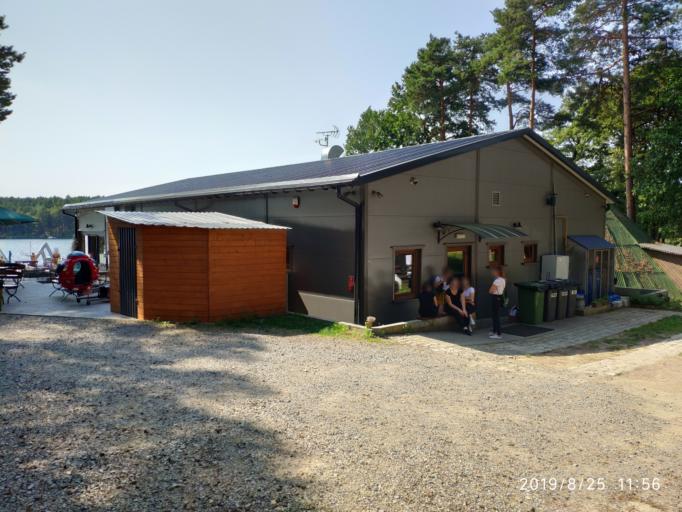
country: PL
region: Lubusz
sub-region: Powiat krosnienski
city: Dabie
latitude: 51.9988
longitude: 15.1544
